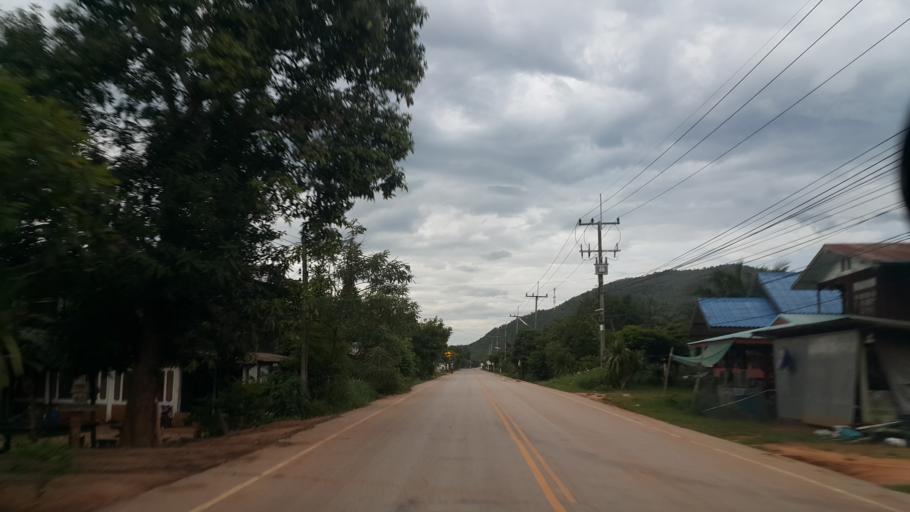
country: TH
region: Loei
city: Na Haeo
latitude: 17.5185
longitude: 101.1779
